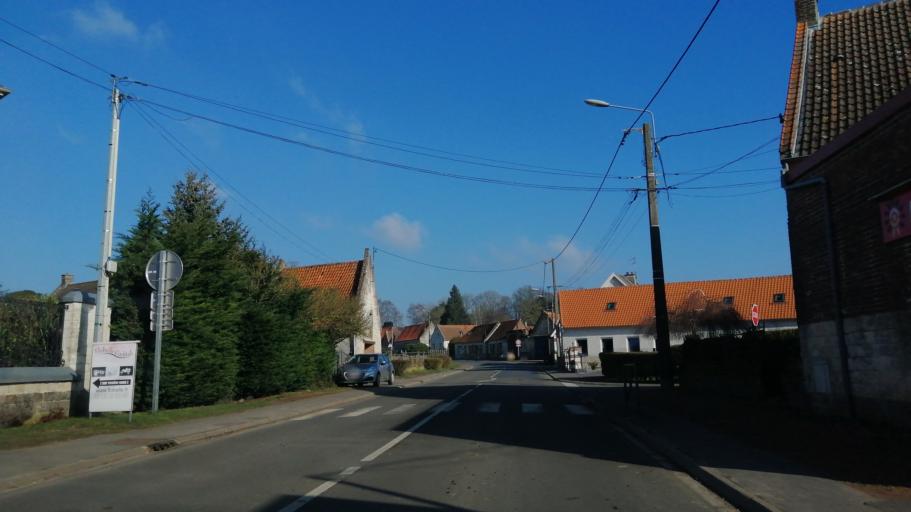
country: FR
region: Nord-Pas-de-Calais
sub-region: Departement du Pas-de-Calais
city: Aubigny-en-Artois
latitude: 50.3742
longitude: 2.6353
